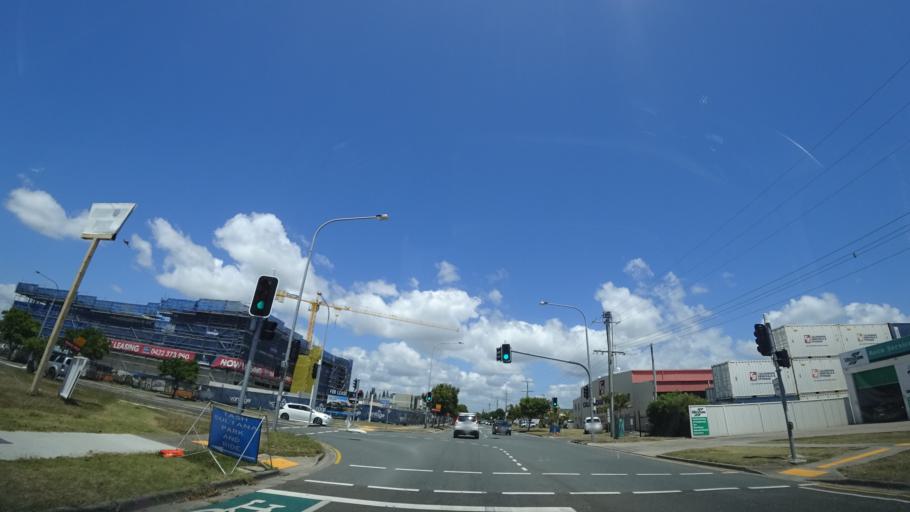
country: AU
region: Queensland
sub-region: Sunshine Coast
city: Mooloolaba
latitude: -26.7308
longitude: 153.1254
